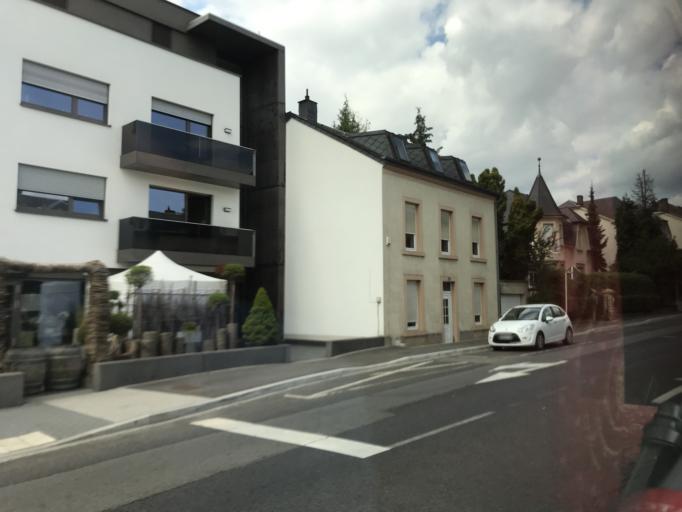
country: LU
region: Luxembourg
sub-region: Canton de Luxembourg
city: Hesperange
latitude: 49.5848
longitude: 6.1454
